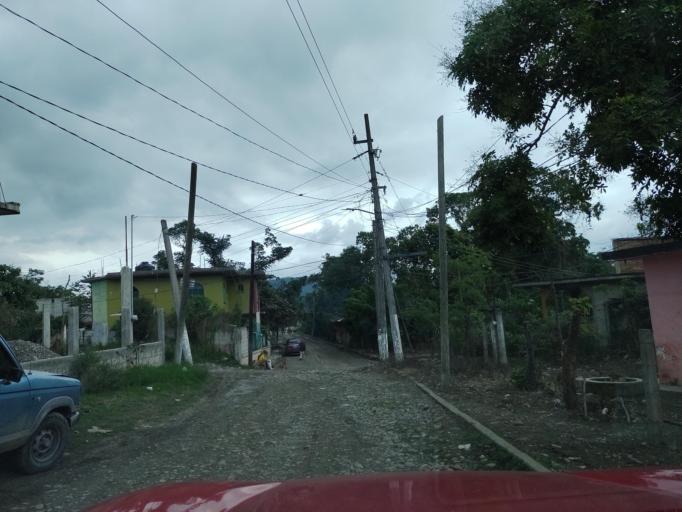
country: MX
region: Veracruz
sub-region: Papantla
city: El Chote
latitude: 20.4289
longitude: -97.3849
